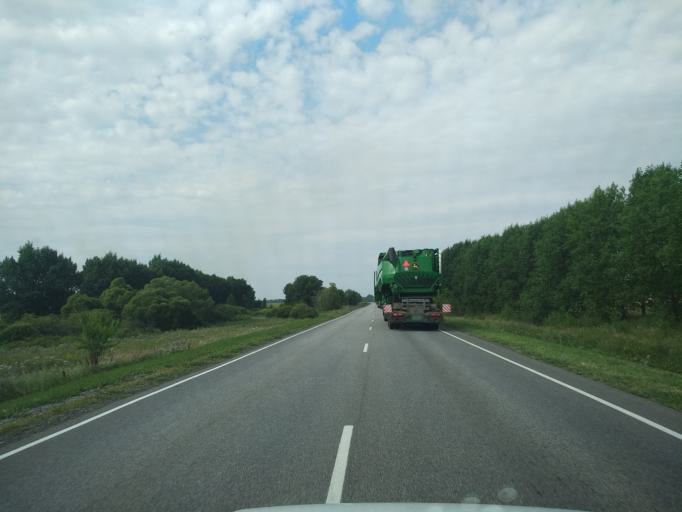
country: RU
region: Voronezj
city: Pereleshinskiy
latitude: 51.8748
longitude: 40.4046
